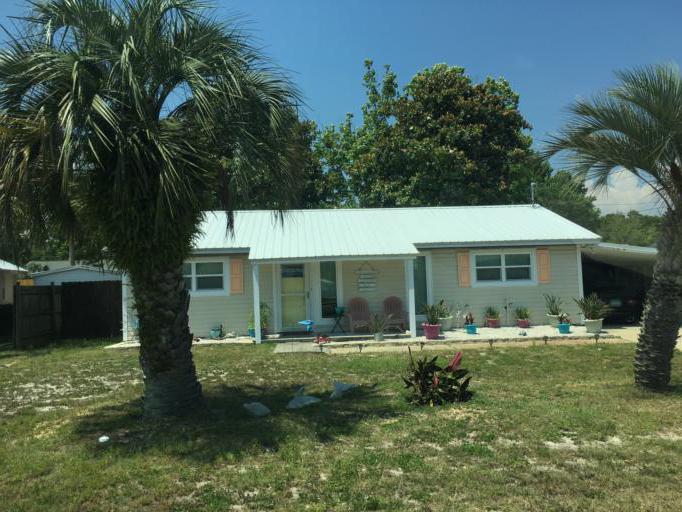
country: US
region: Florida
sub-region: Bay County
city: Laguna Beach
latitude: 30.2349
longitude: -85.8934
